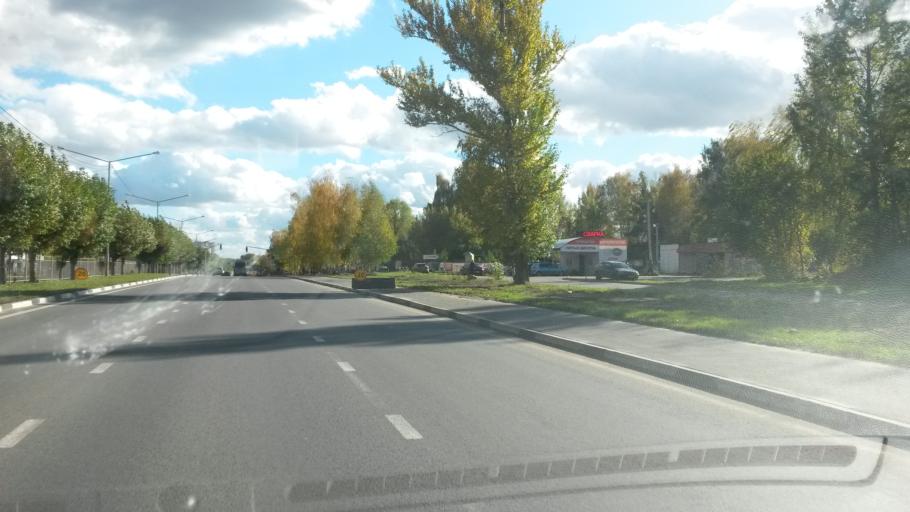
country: RU
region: Jaroslavl
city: Yaroslavl
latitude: 57.5788
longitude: 39.9138
